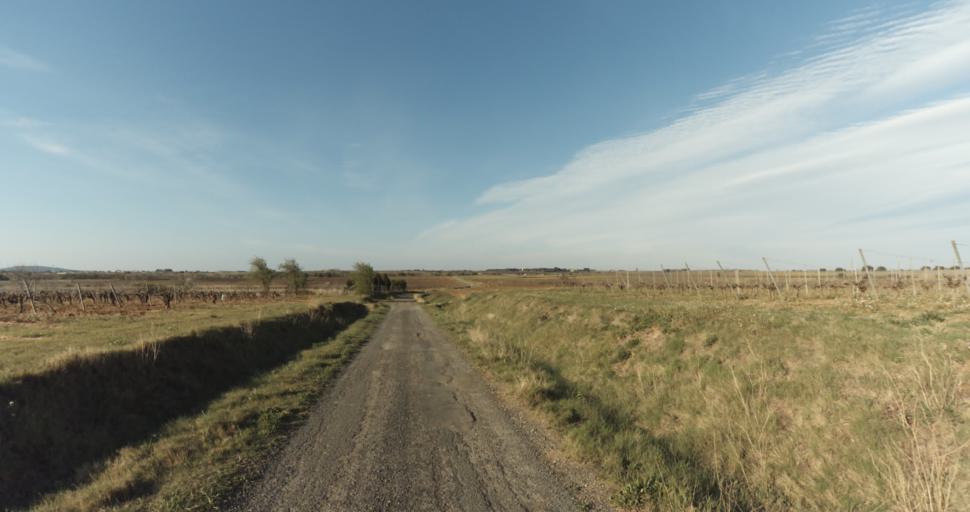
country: FR
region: Languedoc-Roussillon
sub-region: Departement de l'Herault
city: Marseillan
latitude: 43.3780
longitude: 3.5267
